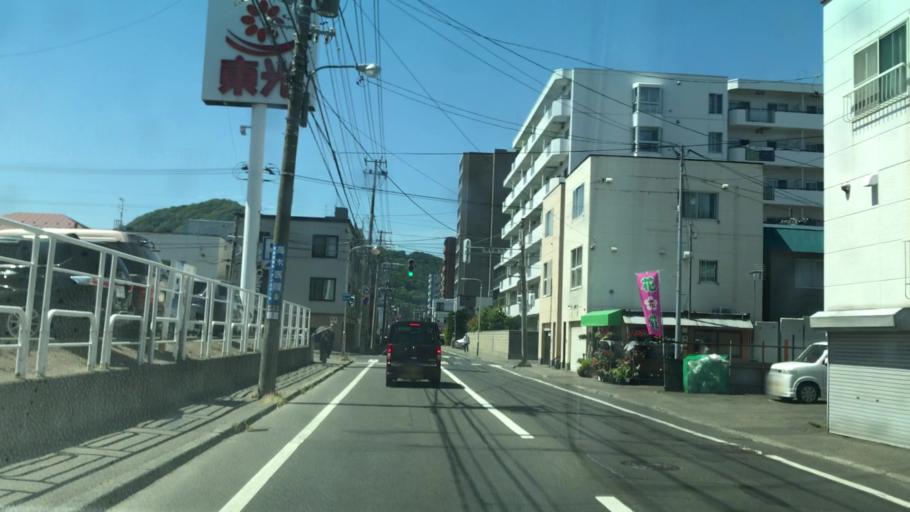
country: JP
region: Hokkaido
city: Sapporo
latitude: 43.0513
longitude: 141.3340
